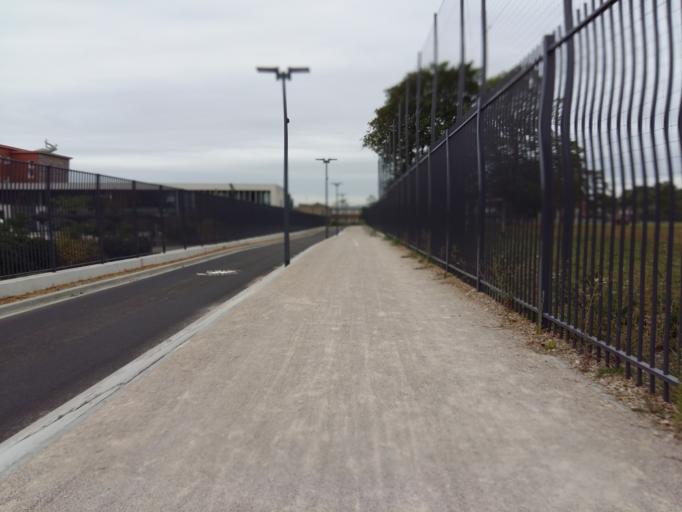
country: FR
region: Picardie
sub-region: Departement de la Somme
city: Amiens
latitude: 49.8763
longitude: 2.2992
